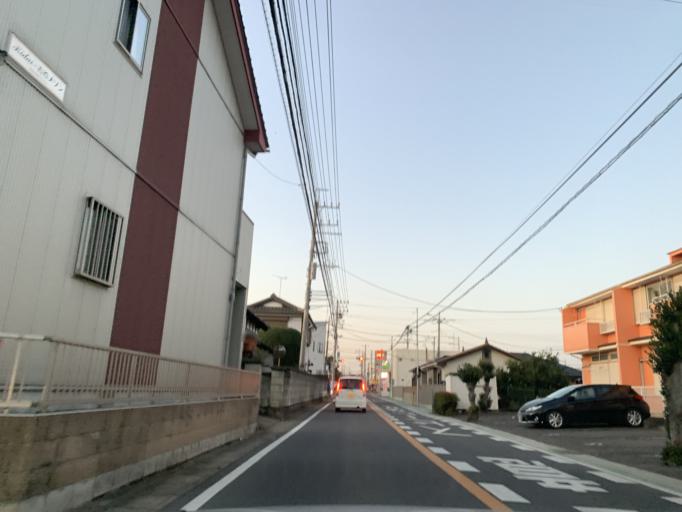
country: JP
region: Chiba
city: Nagareyama
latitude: 35.9072
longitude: 139.9039
